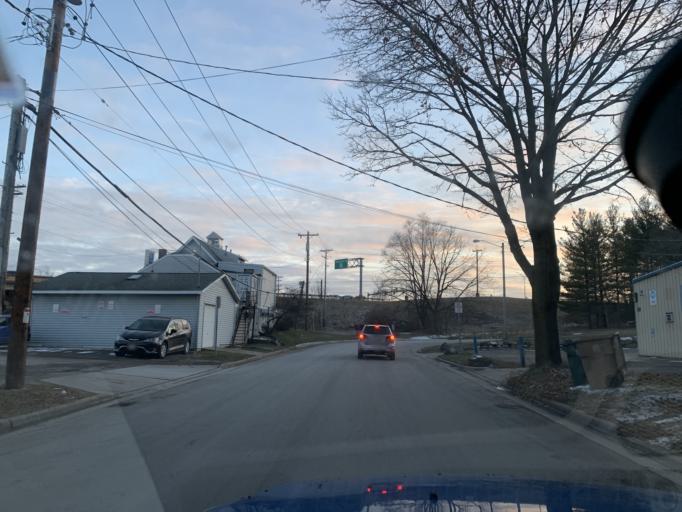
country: US
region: Wisconsin
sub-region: Dane County
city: Shorewood Hills
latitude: 43.0324
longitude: -89.4606
